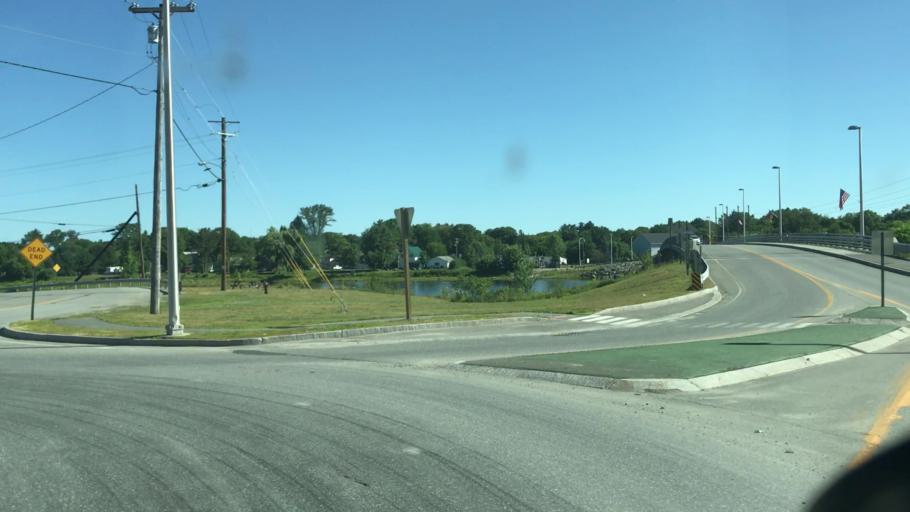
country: US
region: Maine
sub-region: Penobscot County
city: Howland
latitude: 45.2385
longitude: -68.6600
